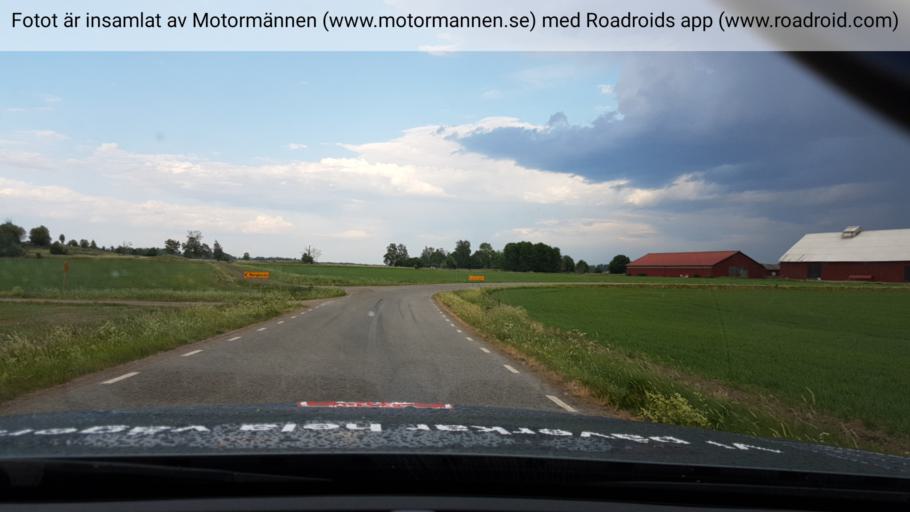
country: SE
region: Vaestmanland
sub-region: Vasteras
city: Skultuna
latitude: 59.7085
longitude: 16.4526
